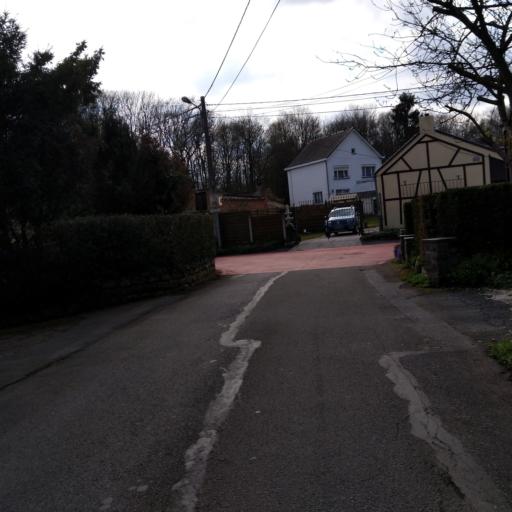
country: BE
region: Wallonia
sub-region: Province du Hainaut
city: Mons
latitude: 50.5073
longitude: 3.9982
